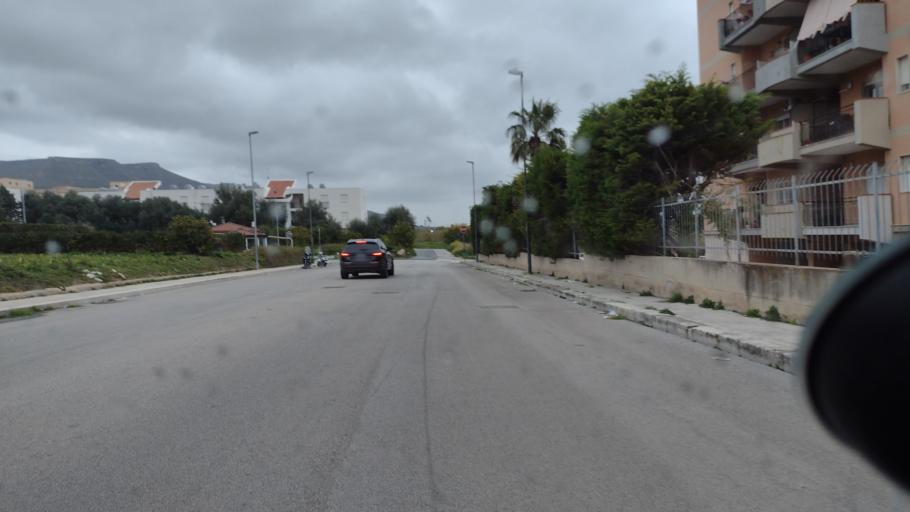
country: IT
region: Sicily
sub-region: Provincia di Siracusa
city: Avola
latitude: 36.9176
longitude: 15.1408
